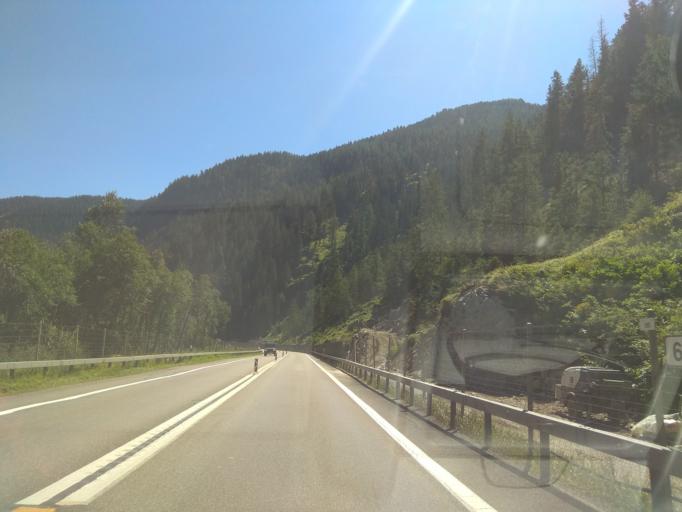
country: CH
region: Grisons
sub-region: Hinterrhein District
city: Thusis
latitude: 46.5669
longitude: 9.3941
